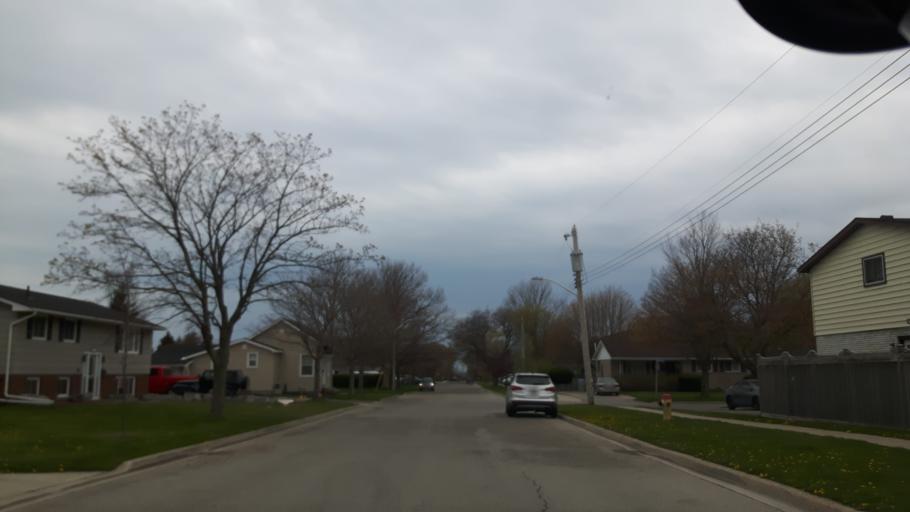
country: CA
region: Ontario
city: Goderich
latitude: 43.7336
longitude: -81.7189
